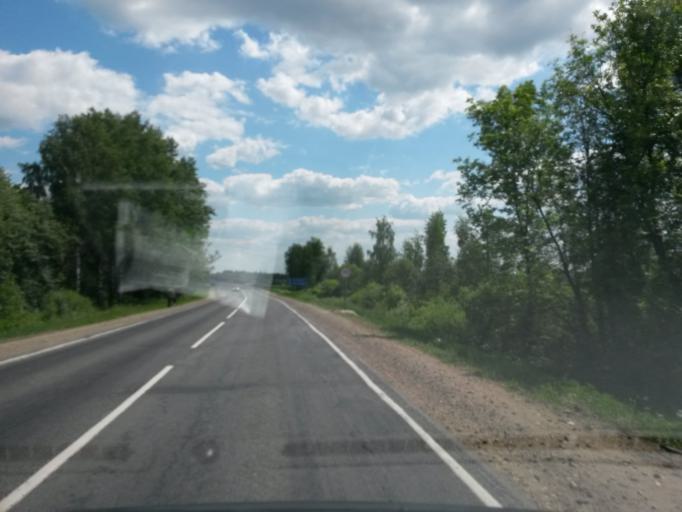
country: RU
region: Jaroslavl
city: Yaroslavl
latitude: 57.5523
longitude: 39.8837
